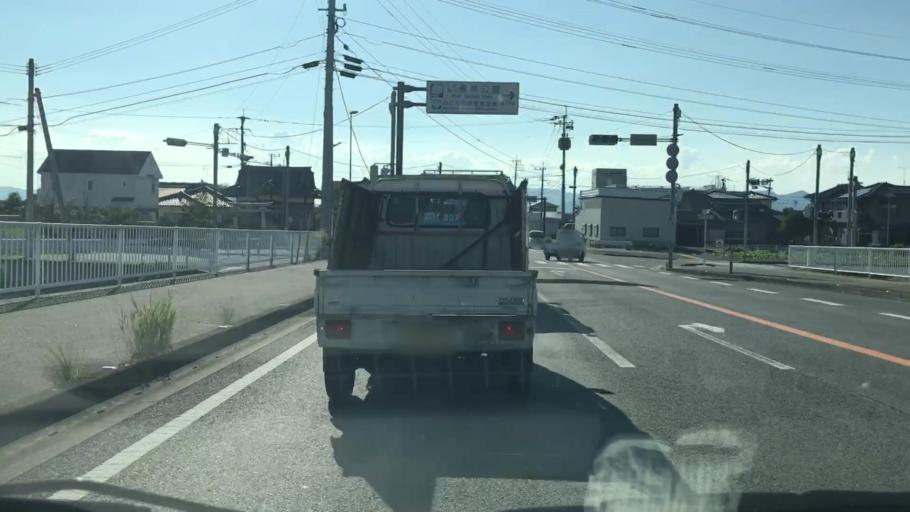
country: JP
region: Saga Prefecture
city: Saga-shi
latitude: 33.2191
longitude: 130.2582
